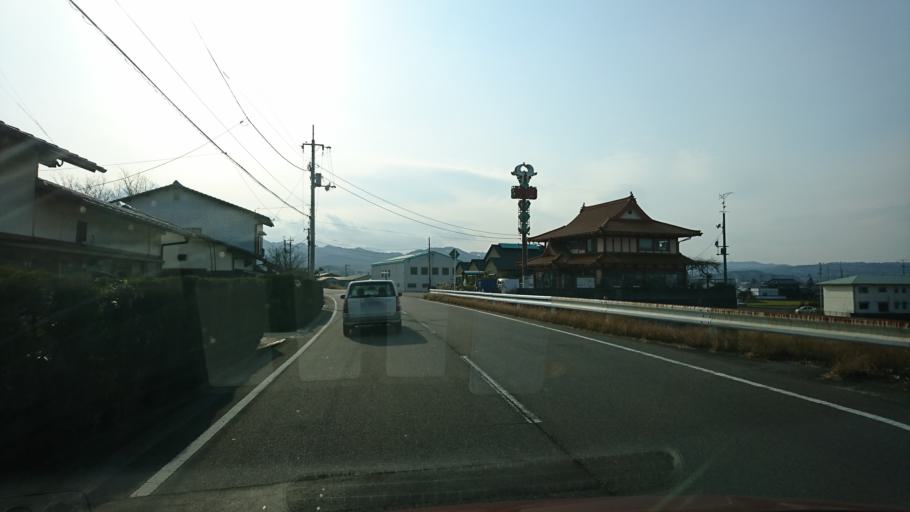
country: JP
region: Ehime
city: Saijo
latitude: 34.0320
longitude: 133.0176
